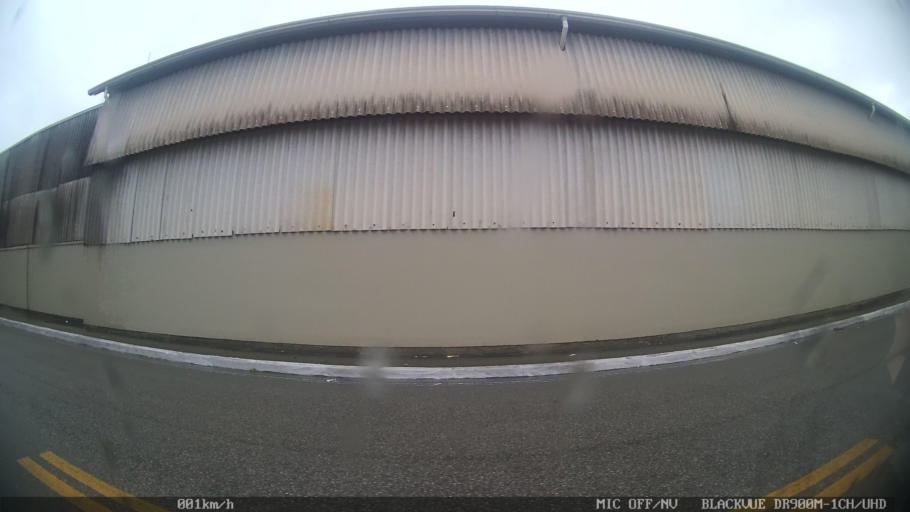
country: BR
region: Santa Catarina
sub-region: Sao Jose
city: Campinas
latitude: -27.5991
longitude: -48.6180
